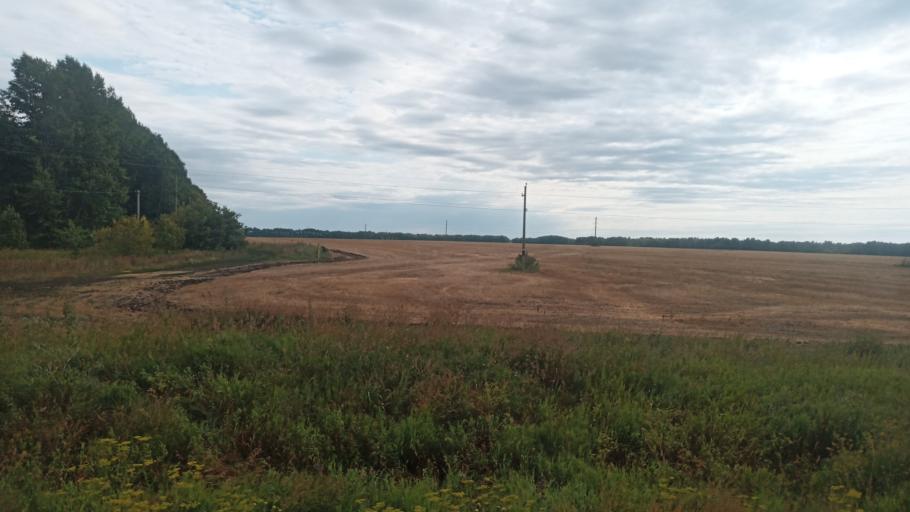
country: RU
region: Altai Krai
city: Nalobikha
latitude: 53.2402
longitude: 84.4568
